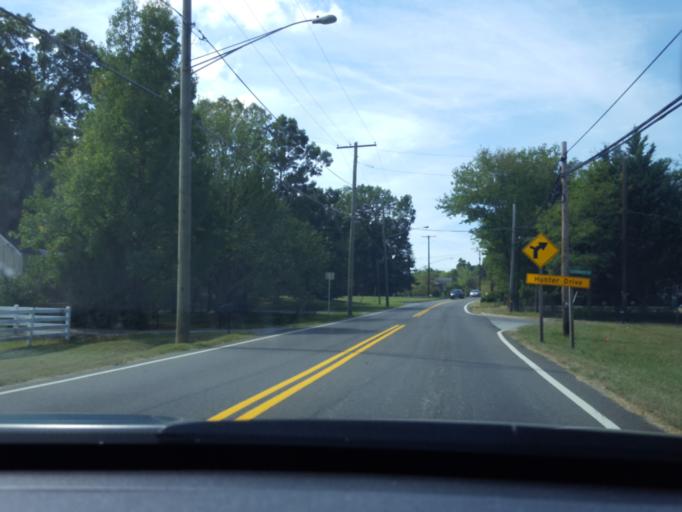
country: US
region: Maryland
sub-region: Prince George's County
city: Andrews AFB
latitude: 38.7807
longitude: -76.8537
